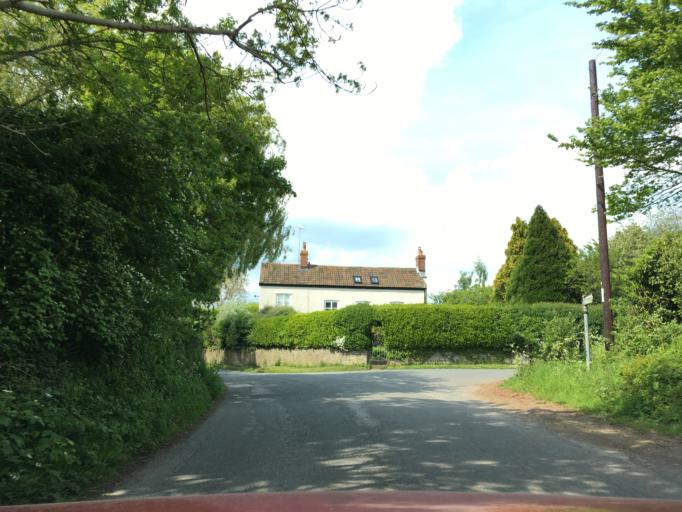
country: GB
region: England
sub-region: South Gloucestershire
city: Thornbury
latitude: 51.6114
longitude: -2.5497
